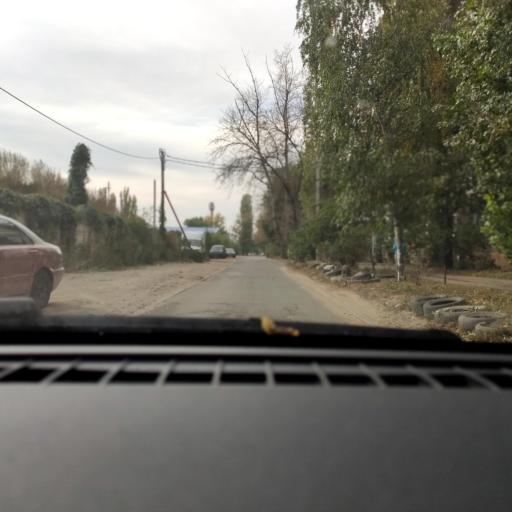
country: RU
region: Voronezj
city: Maslovka
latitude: 51.6388
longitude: 39.2742
